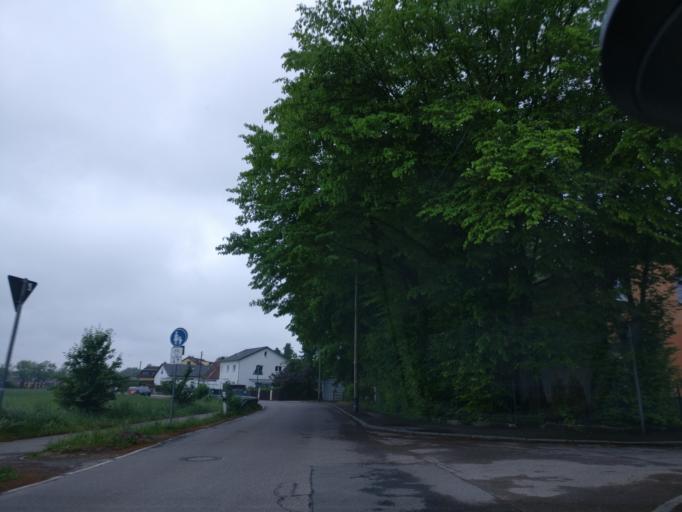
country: DE
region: Bavaria
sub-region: Upper Bavaria
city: Grobenzell
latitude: 48.1822
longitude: 11.4082
